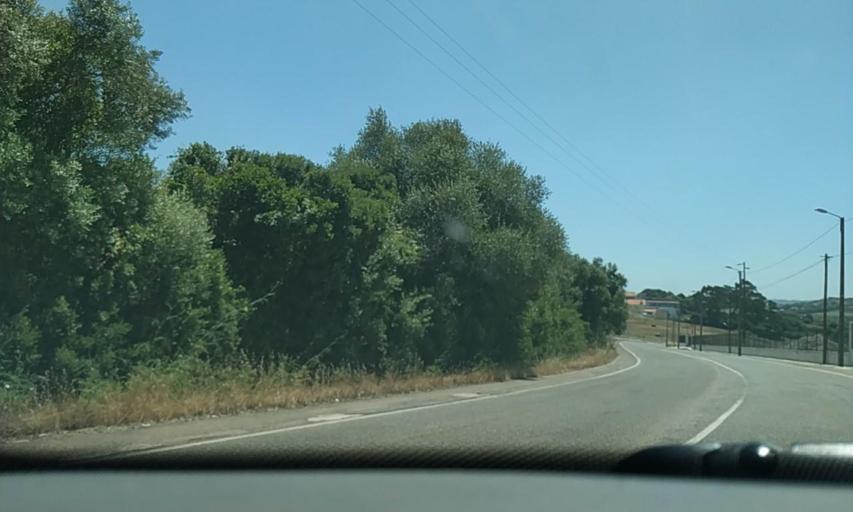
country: PT
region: Lisbon
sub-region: Sintra
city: Almargem
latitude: 38.8726
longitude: -9.2858
